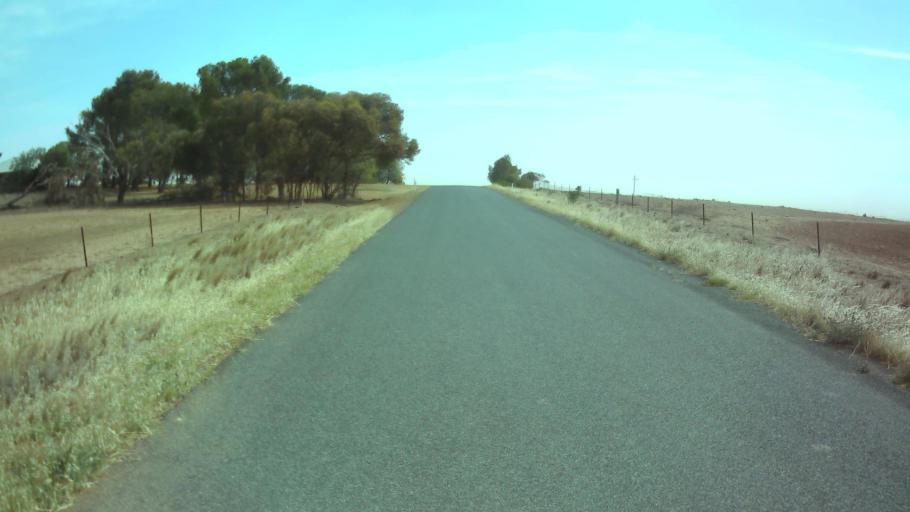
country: AU
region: New South Wales
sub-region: Weddin
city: Grenfell
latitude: -33.7312
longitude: 147.9979
